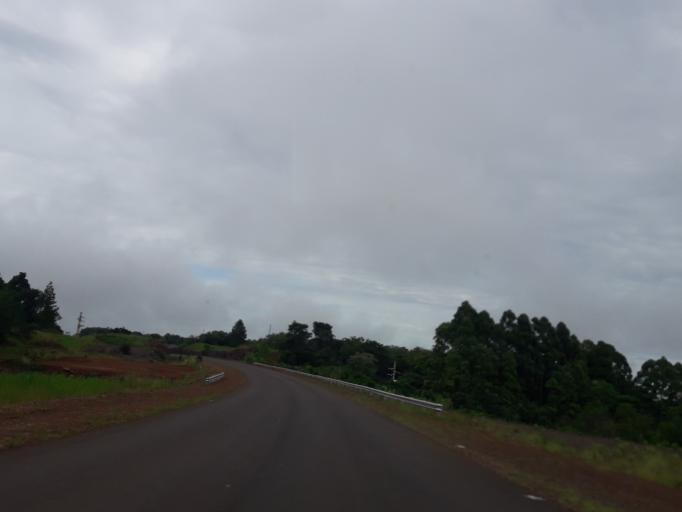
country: AR
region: Misiones
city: Bernardo de Irigoyen
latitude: -26.4275
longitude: -53.8484
